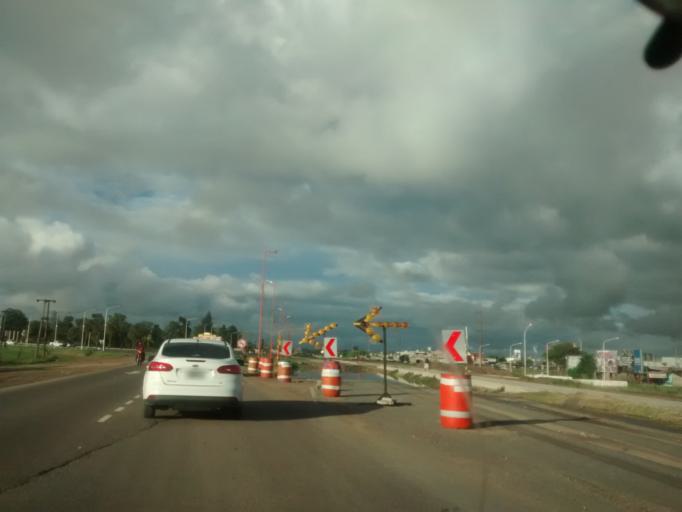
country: AR
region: Chaco
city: Fontana
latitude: -27.4476
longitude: -59.0254
